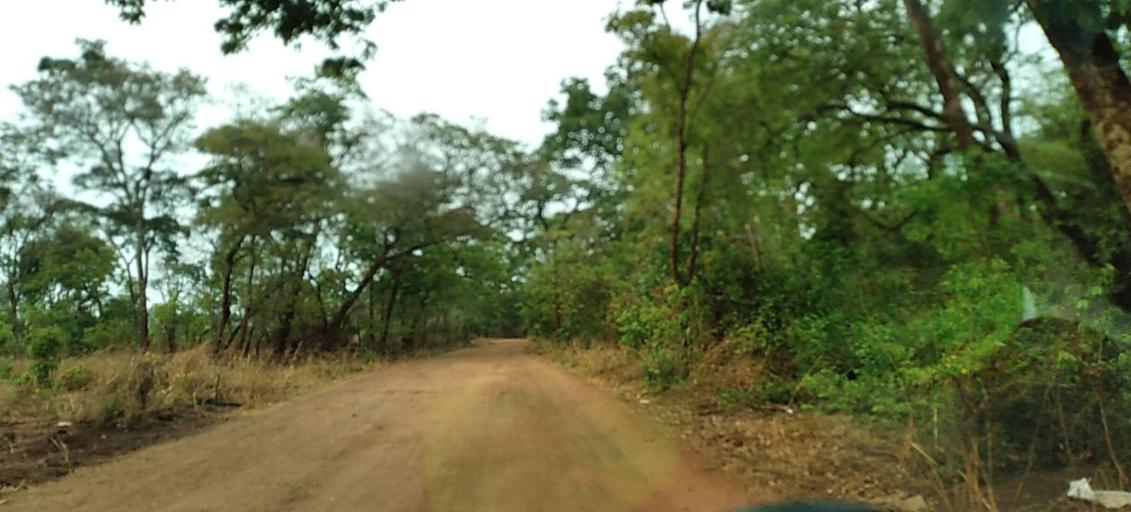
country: ZM
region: North-Western
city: Solwezi
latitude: -12.3084
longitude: 26.5226
